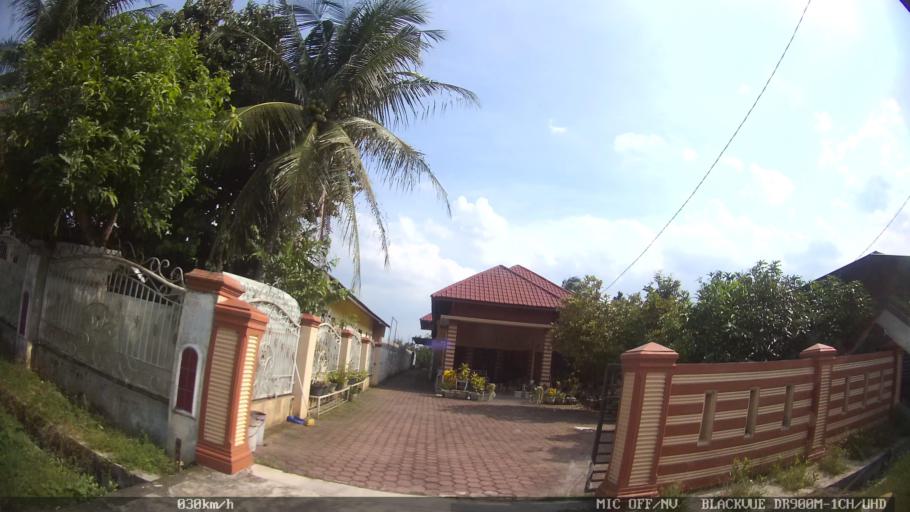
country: ID
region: North Sumatra
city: Binjai
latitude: 3.6437
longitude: 98.5136
